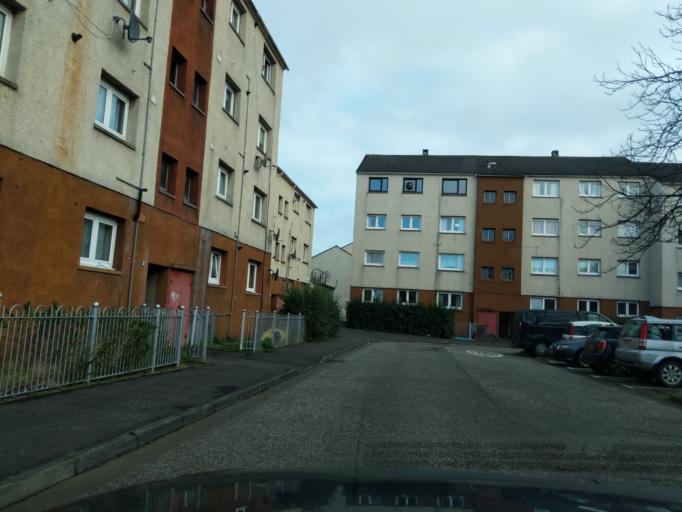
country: GB
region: Scotland
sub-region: Edinburgh
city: Colinton
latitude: 55.9184
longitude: -3.2780
